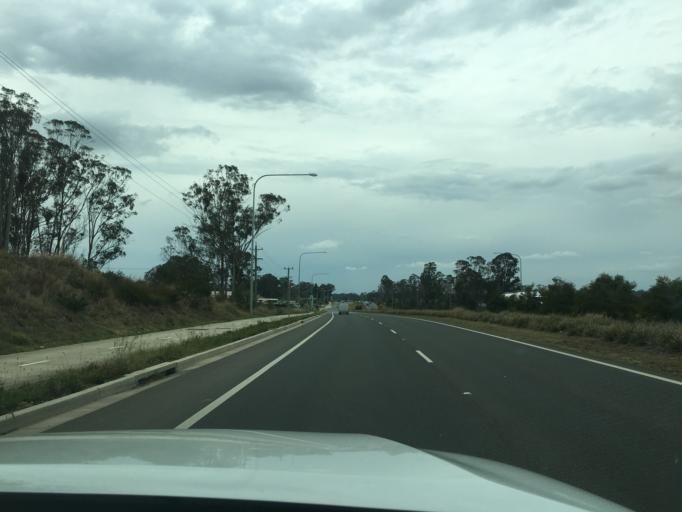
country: AU
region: New South Wales
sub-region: Campbelltown Municipality
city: Denham Court
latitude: -33.9742
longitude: 150.8109
